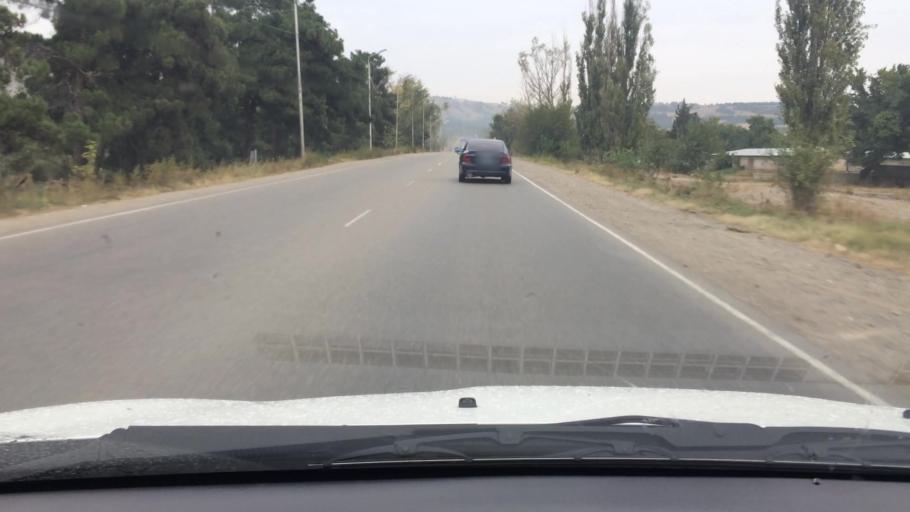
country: GE
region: T'bilisi
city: Tbilisi
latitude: 41.6089
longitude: 44.7851
